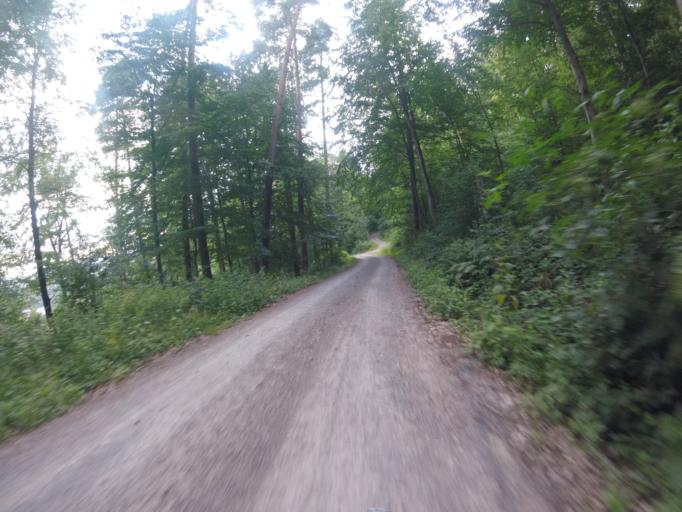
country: DE
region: Baden-Wuerttemberg
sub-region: Regierungsbezirk Stuttgart
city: Oppenweiler
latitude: 48.9681
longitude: 9.4911
